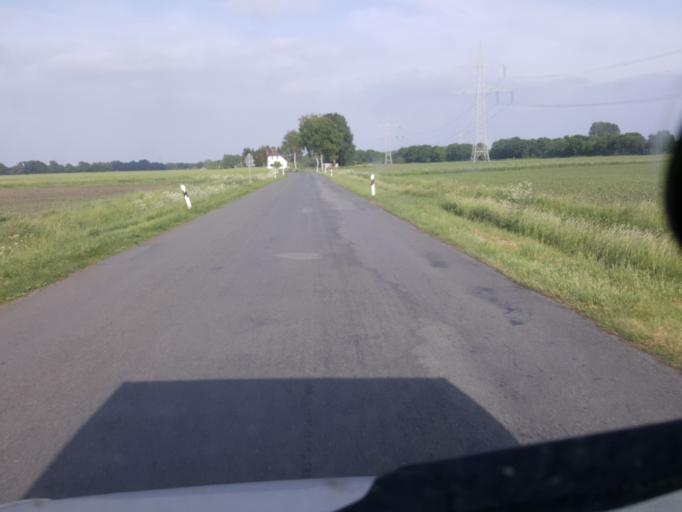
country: DE
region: Lower Saxony
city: Uchte
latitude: 52.5467
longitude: 8.9571
